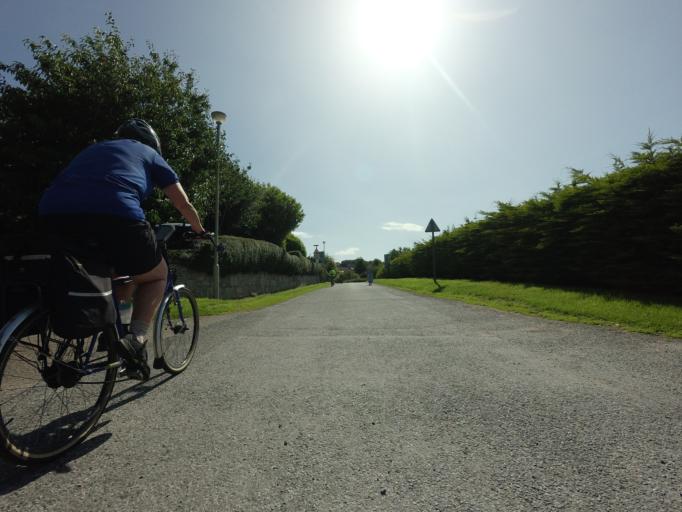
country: GB
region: Scotland
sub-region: Highland
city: Inverness
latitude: 57.4749
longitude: -4.1614
